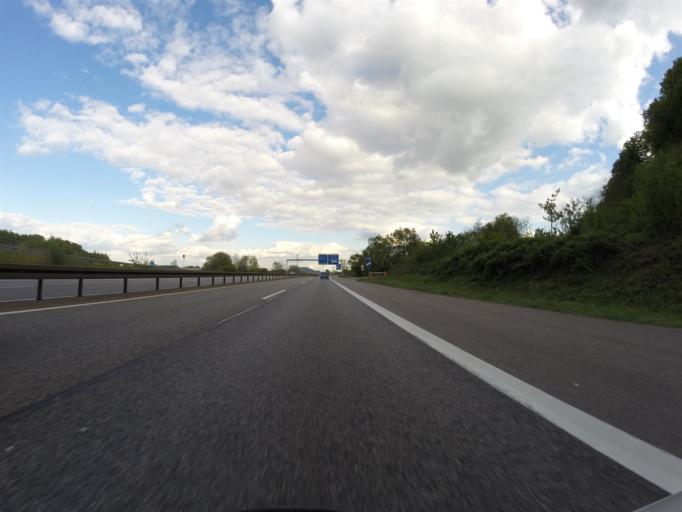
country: DE
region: Saarland
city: Wallerfangen
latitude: 49.3386
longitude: 6.7156
